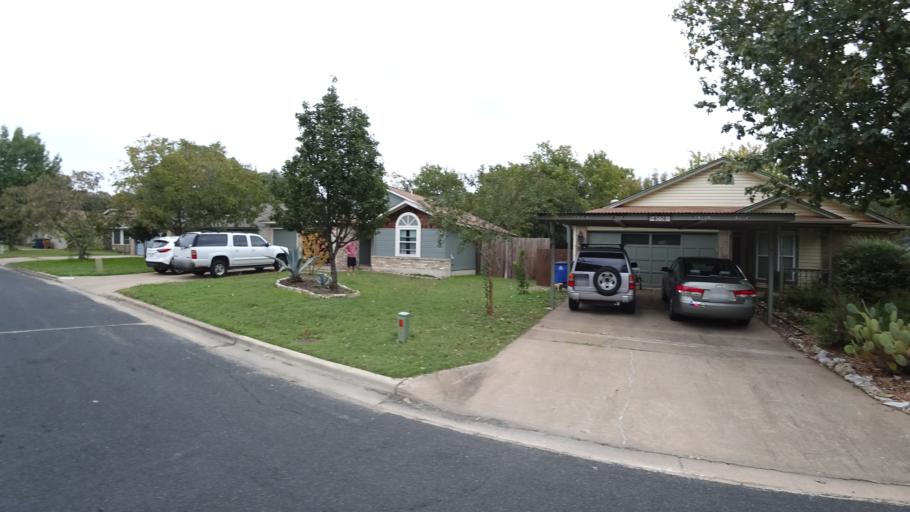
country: US
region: Texas
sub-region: Travis County
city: Shady Hollow
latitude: 30.2095
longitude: -97.8428
